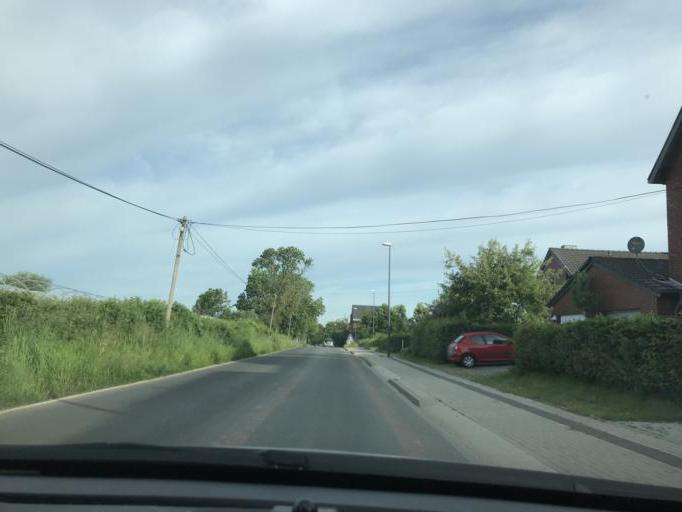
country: DE
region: North Rhine-Westphalia
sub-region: Regierungsbezirk Koln
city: Aachen
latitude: 50.7473
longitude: 6.1404
